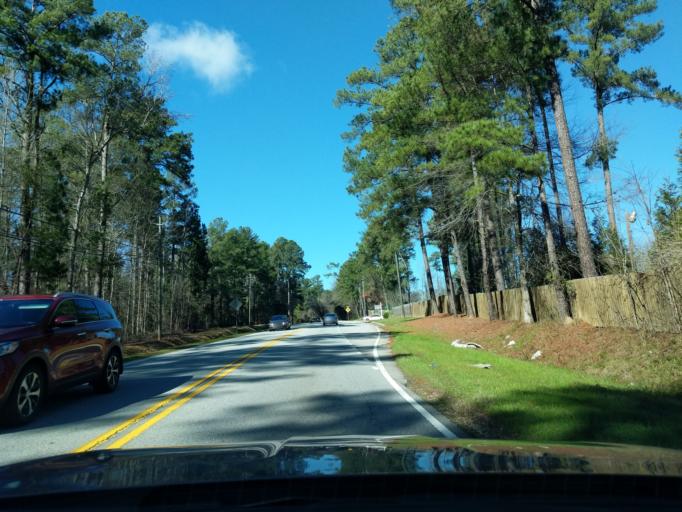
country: US
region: Georgia
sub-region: Columbia County
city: Evans
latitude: 33.5291
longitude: -82.1899
